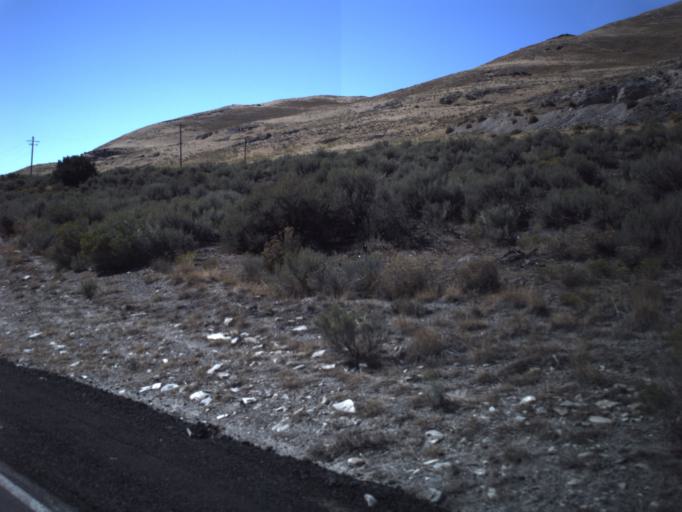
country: US
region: Utah
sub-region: Utah County
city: Saratoga Springs
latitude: 40.2498
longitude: -111.8661
